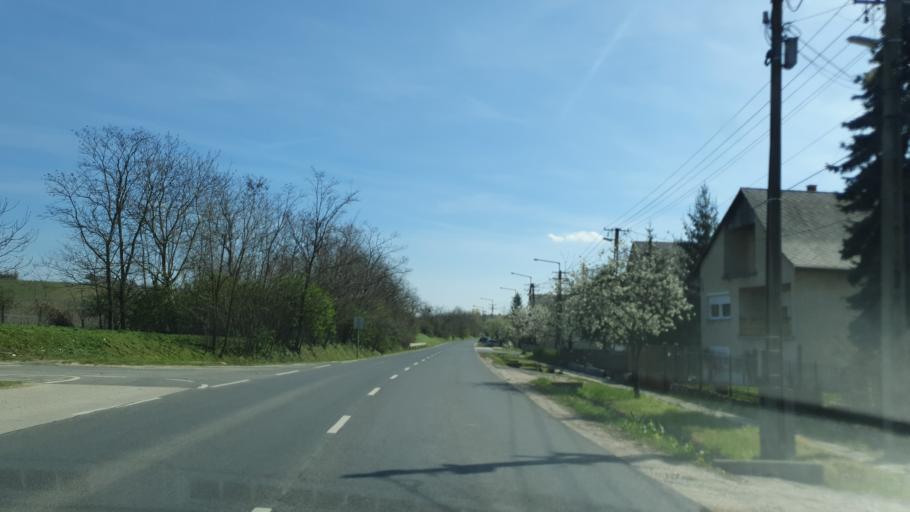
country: HU
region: Fejer
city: Mor
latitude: 47.3847
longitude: 18.2259
